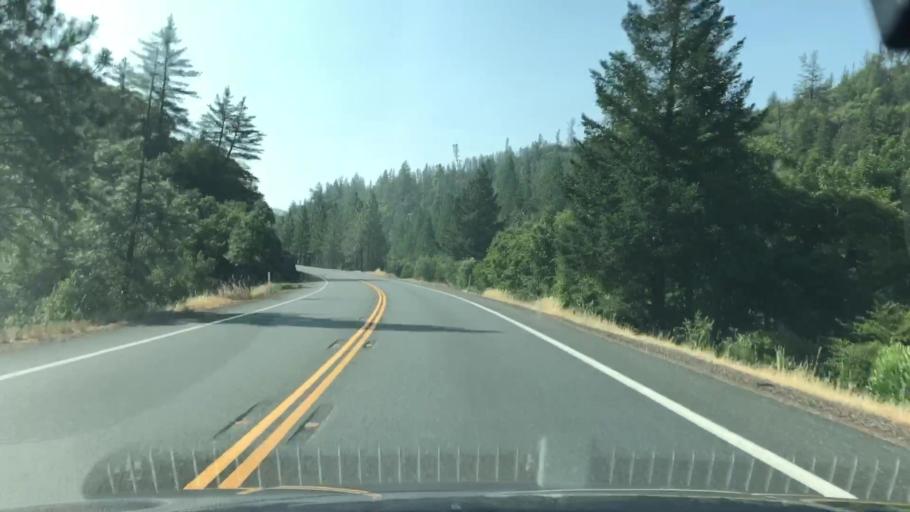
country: US
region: California
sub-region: Lake County
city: Middletown
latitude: 38.6912
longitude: -122.5977
